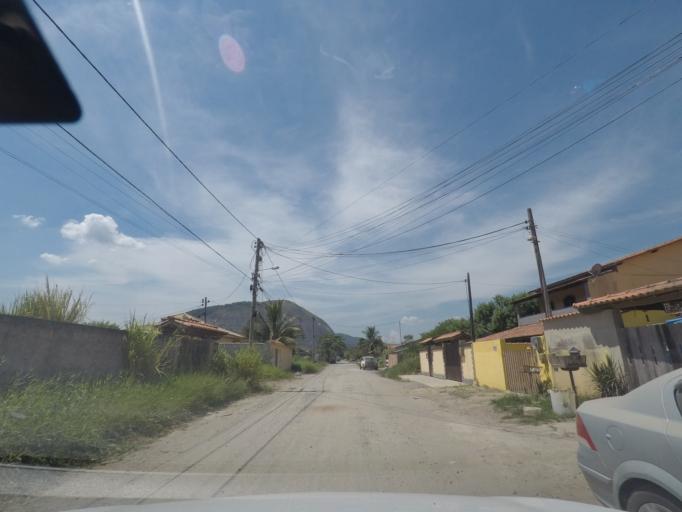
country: BR
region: Rio de Janeiro
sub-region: Marica
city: Marica
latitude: -22.9584
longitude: -42.9577
